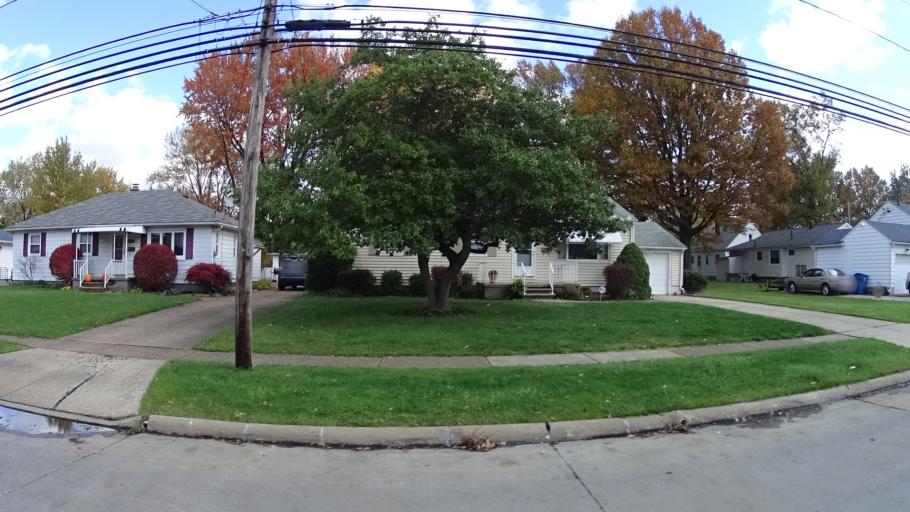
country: US
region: Ohio
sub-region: Lorain County
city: Lorain
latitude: 41.4374
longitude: -82.1897
